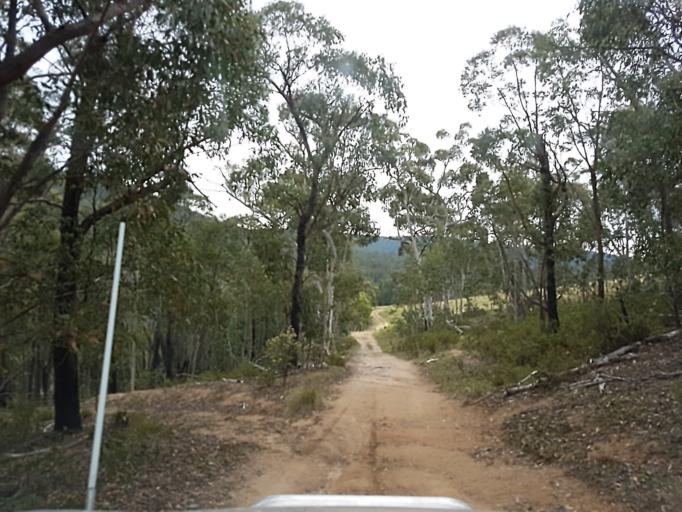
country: AU
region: New South Wales
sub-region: Snowy River
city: Jindabyne
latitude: -36.8673
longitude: 148.3282
